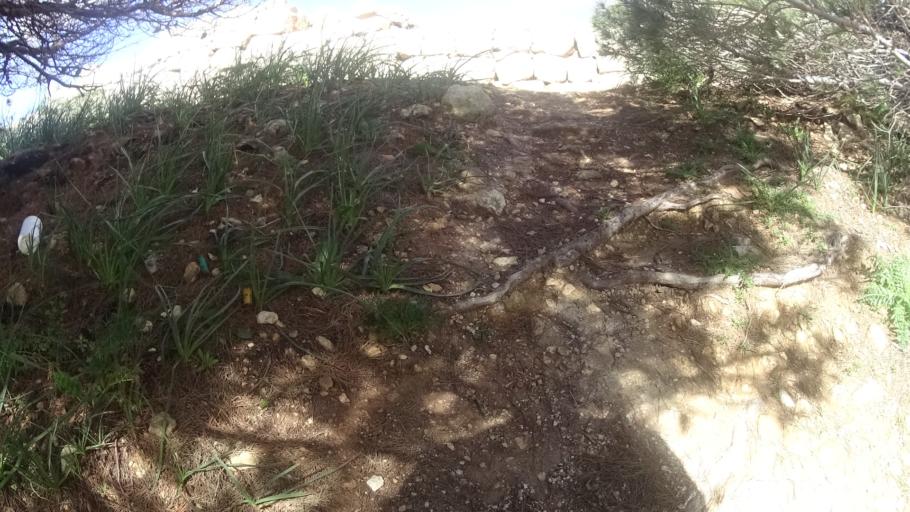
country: MT
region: L-Imgarr
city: Imgarr
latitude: 35.9054
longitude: 14.3798
